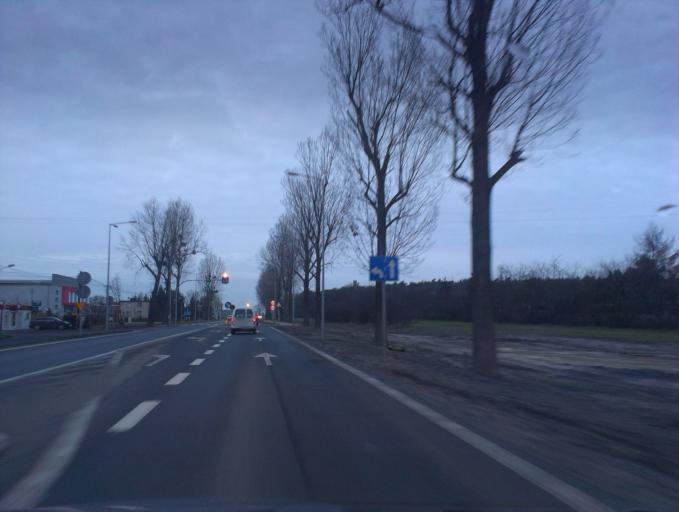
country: PL
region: Greater Poland Voivodeship
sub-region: Powiat poznanski
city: Zlotniki
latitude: 52.4964
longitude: 16.8412
